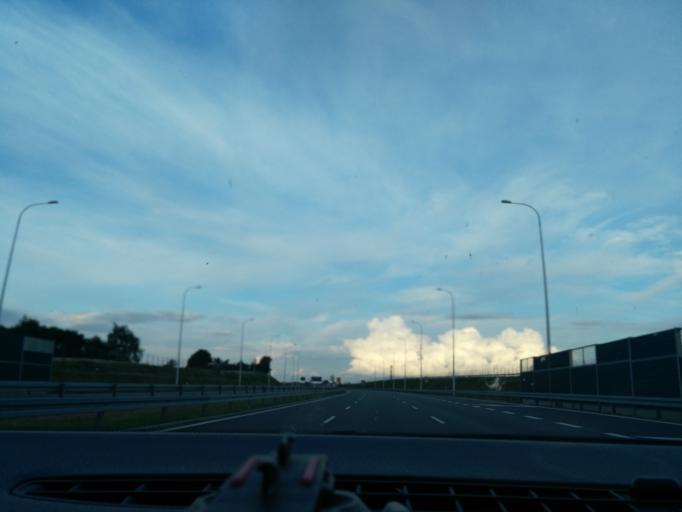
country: PL
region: Lublin Voivodeship
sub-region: Powiat lubelski
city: Lublin
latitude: 51.2989
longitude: 22.5218
